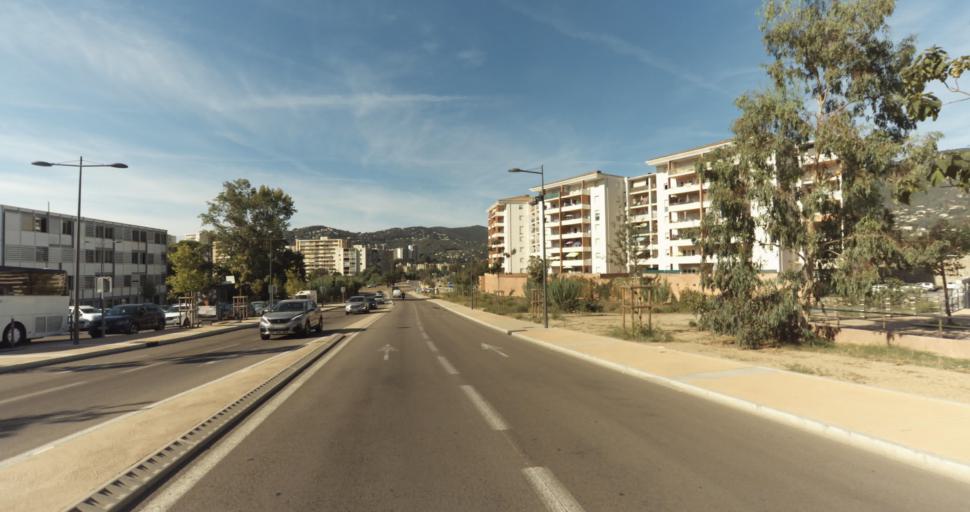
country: FR
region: Corsica
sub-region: Departement de la Corse-du-Sud
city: Ajaccio
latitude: 41.9400
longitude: 8.7438
